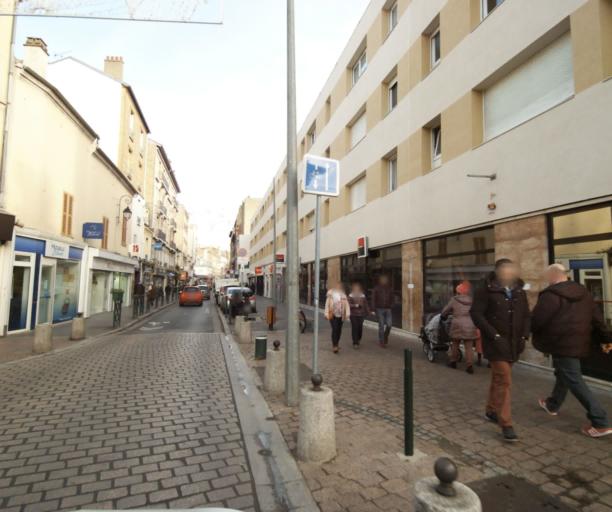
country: FR
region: Ile-de-France
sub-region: Departement des Hauts-de-Seine
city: Nanterre
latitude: 48.8930
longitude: 2.1958
